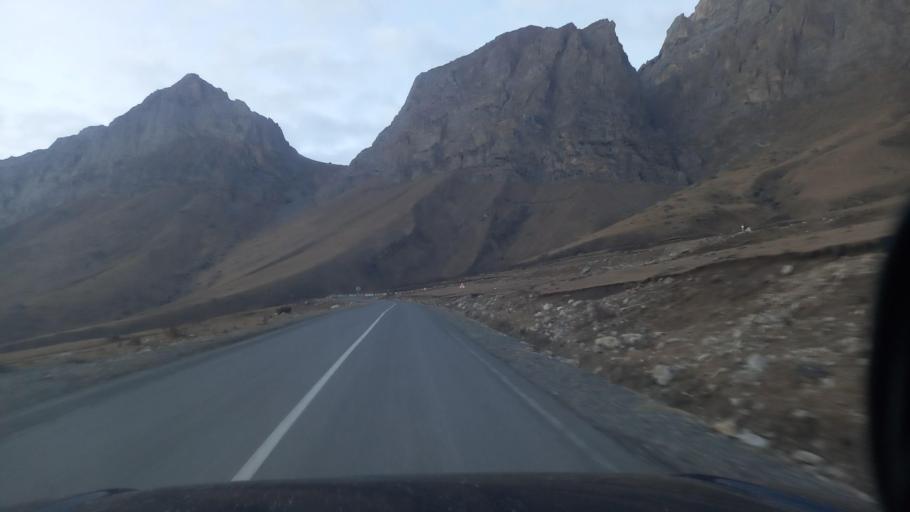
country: RU
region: Ingushetiya
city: Dzhayrakh
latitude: 42.8233
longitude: 44.8252
